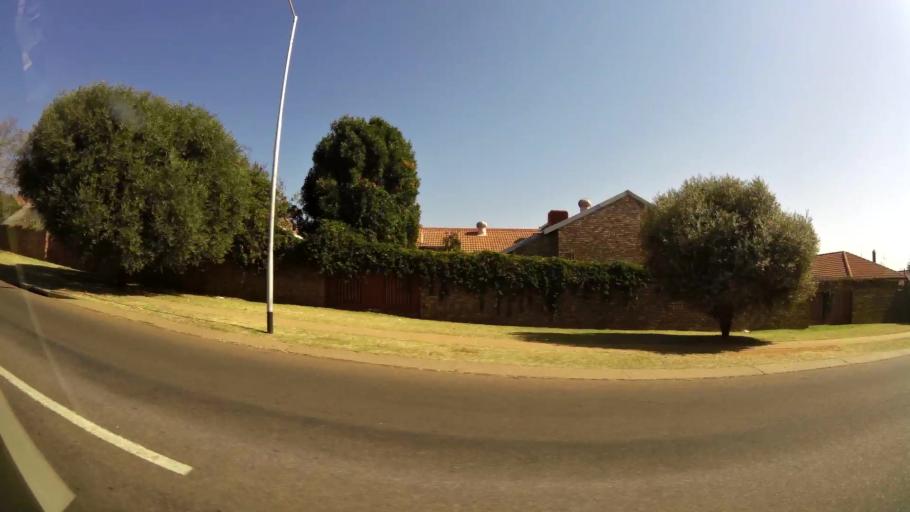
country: ZA
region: Gauteng
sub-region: City of Tshwane Metropolitan Municipality
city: Pretoria
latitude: -25.6831
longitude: 28.2477
